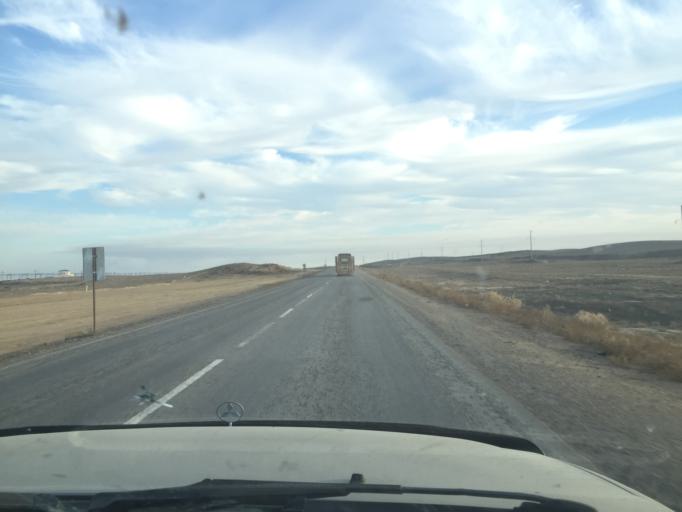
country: KZ
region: Almaty Oblysy
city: Ulken
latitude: 45.1804
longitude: 73.9251
